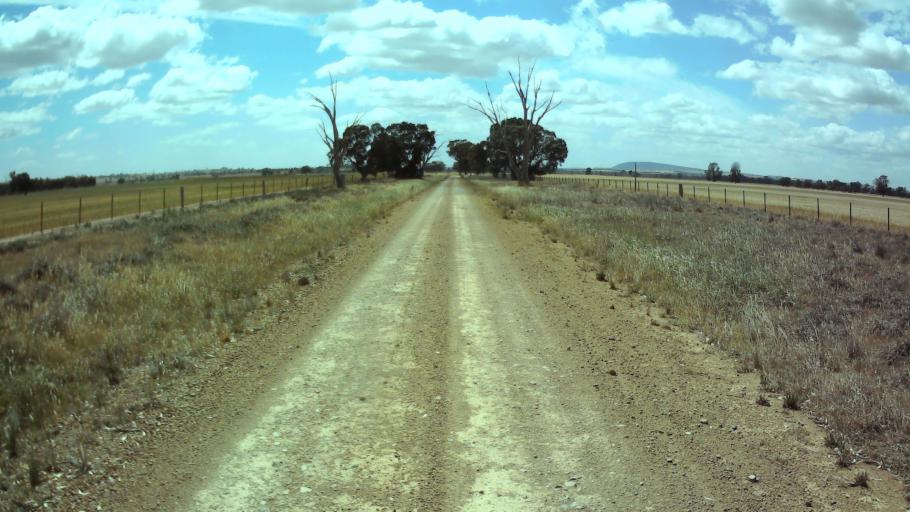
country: AU
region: New South Wales
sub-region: Weddin
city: Grenfell
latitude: -33.9961
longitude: 148.2848
